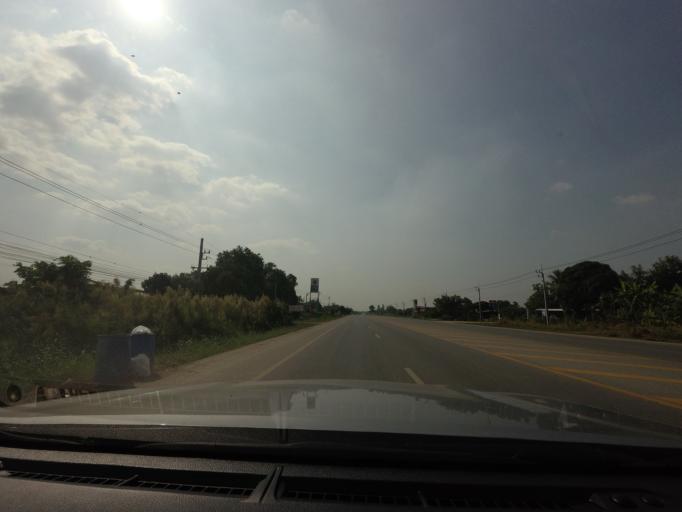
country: TH
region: Phitsanulok
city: Bang Rakam
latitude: 16.7662
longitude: 100.1384
